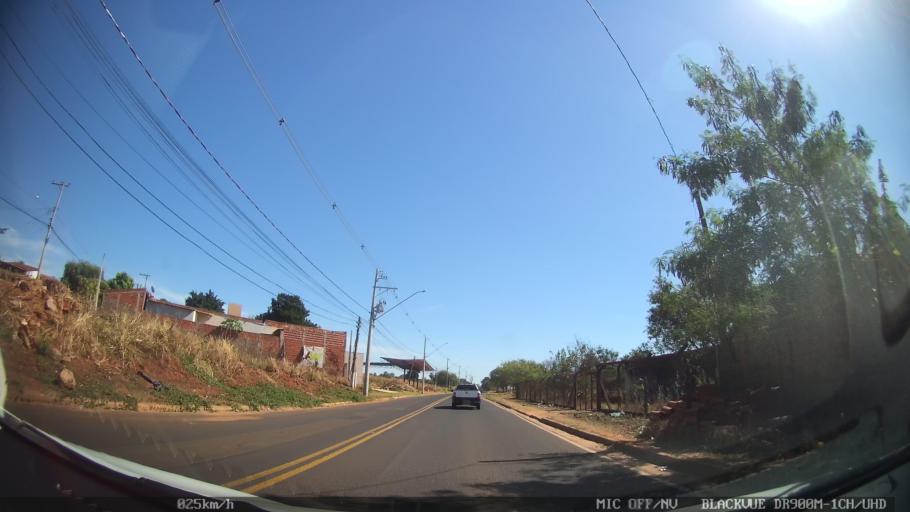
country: BR
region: Sao Paulo
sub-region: Sao Jose Do Rio Preto
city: Sao Jose do Rio Preto
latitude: -20.7630
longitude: -49.4288
